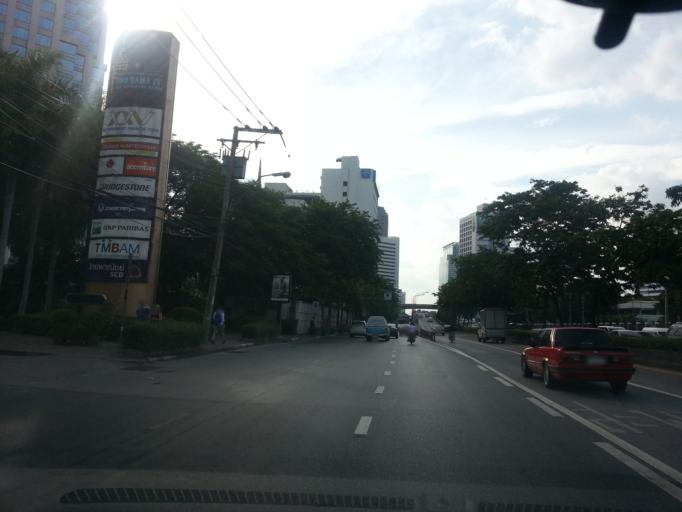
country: TH
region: Bangkok
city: Bang Rak
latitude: 13.7279
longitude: 100.5403
